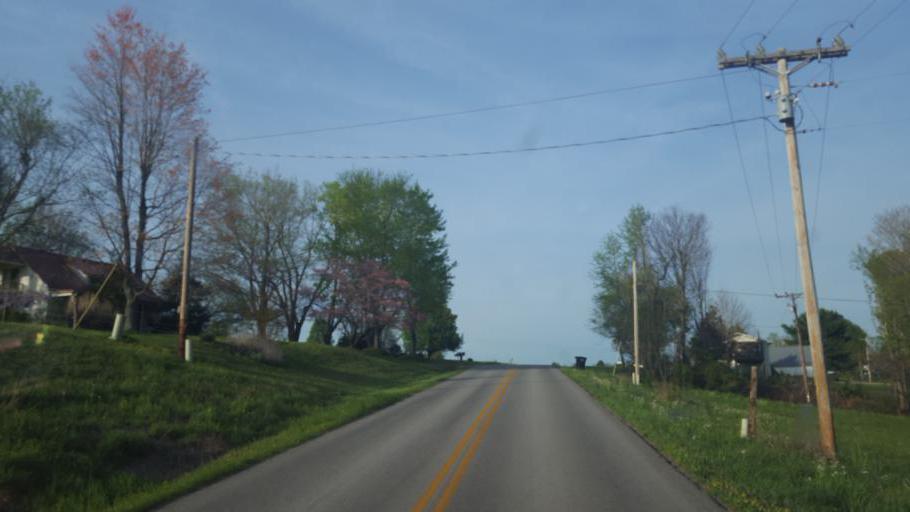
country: US
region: Kentucky
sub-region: Barren County
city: Glasgow
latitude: 36.9451
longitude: -86.0229
